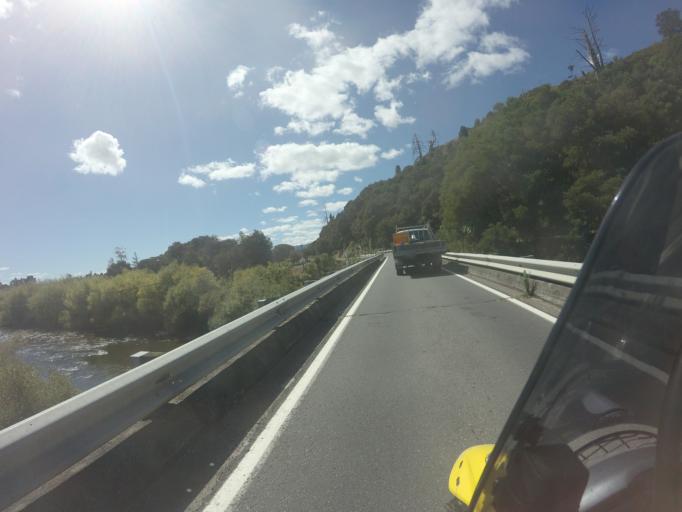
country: NZ
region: Bay of Plenty
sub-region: Whakatane District
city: Murupara
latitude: -38.4784
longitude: 176.7475
